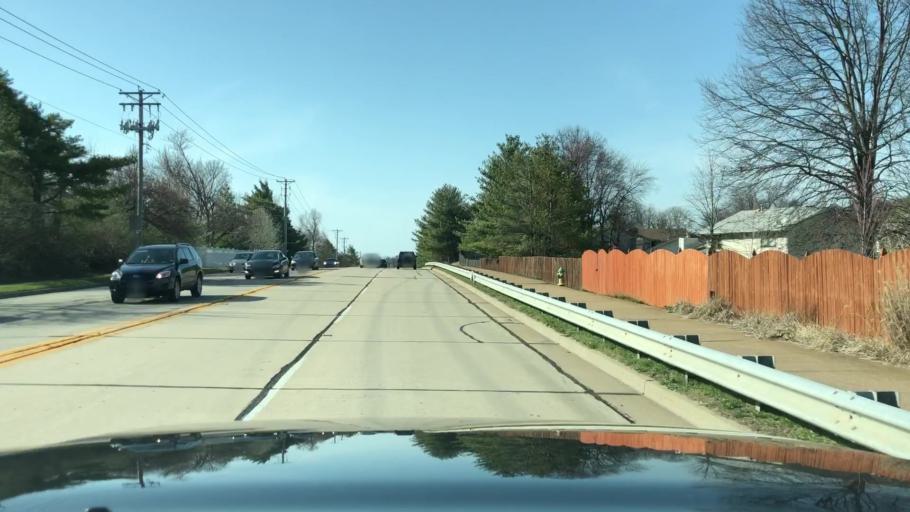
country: US
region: Missouri
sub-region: Saint Charles County
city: Saint Charles
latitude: 38.7738
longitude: -90.5509
